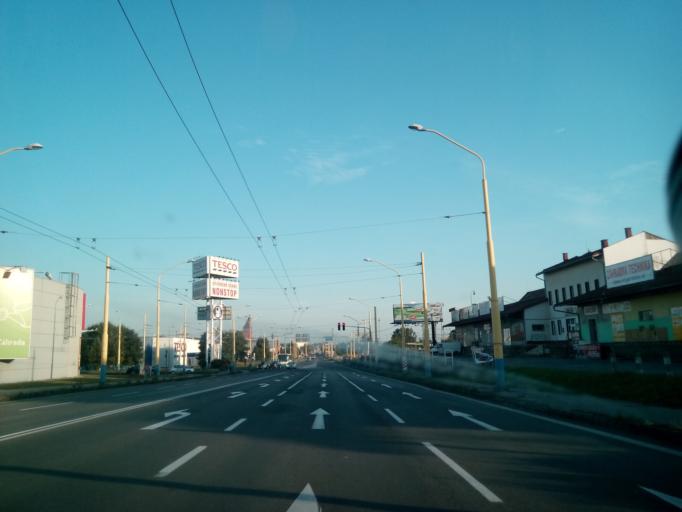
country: SK
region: Presovsky
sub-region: Okres Presov
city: Presov
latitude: 48.9824
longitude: 21.2502
